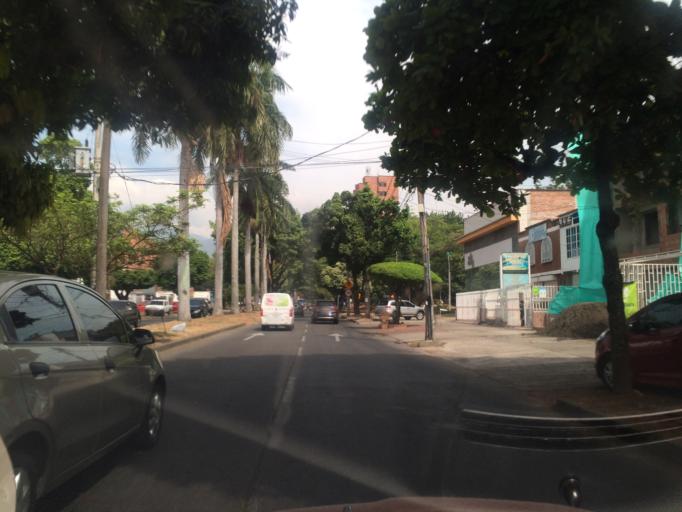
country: CO
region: Valle del Cauca
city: Cali
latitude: 3.4083
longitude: -76.5447
